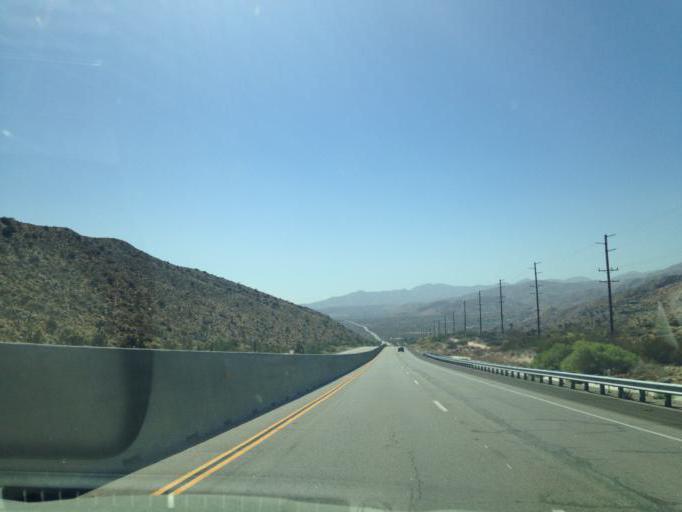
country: US
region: California
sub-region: San Bernardino County
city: Yucca Valley
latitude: 34.1076
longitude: -116.4844
